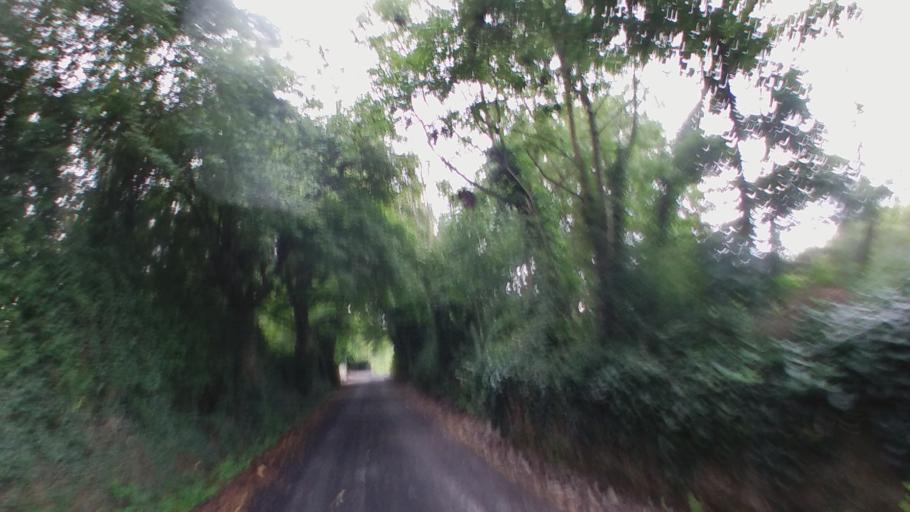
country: IE
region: Leinster
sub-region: Kilkenny
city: Kilkenny
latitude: 52.6862
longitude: -7.2198
